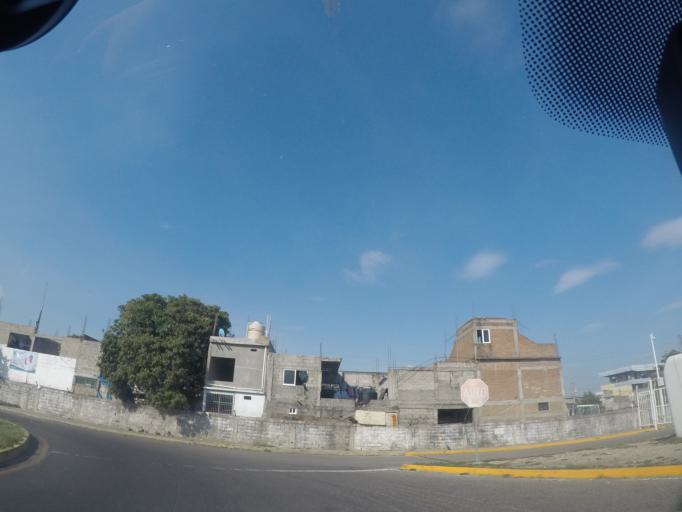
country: MX
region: Oaxaca
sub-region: Salina Cruz
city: Salina Cruz
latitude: 16.1745
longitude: -95.1944
